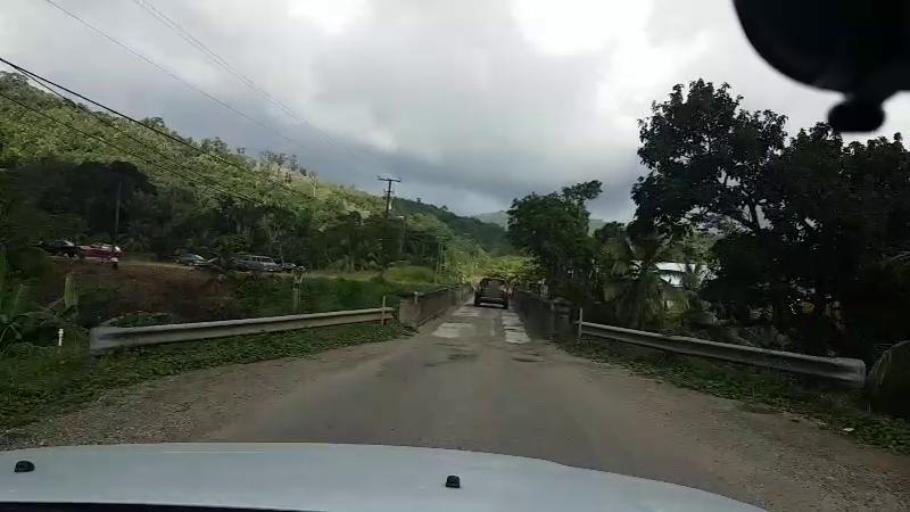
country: BZ
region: Stann Creek
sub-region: Dangriga
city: Dangriga
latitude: 16.9988
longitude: -88.4259
